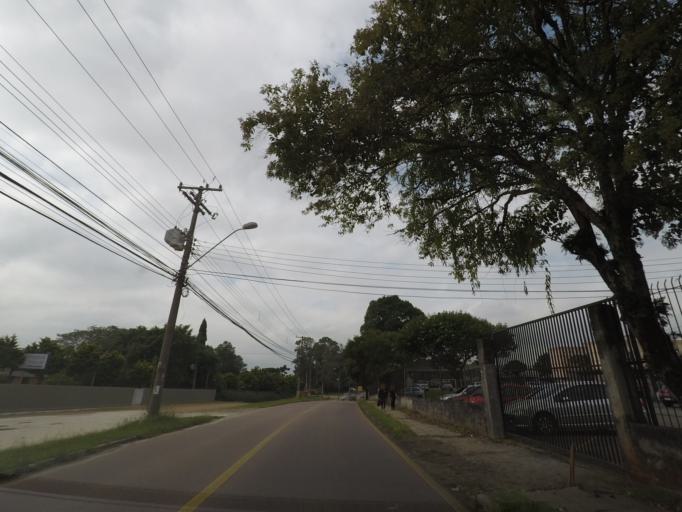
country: BR
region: Parana
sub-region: Curitiba
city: Curitiba
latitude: -25.4943
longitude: -49.3170
